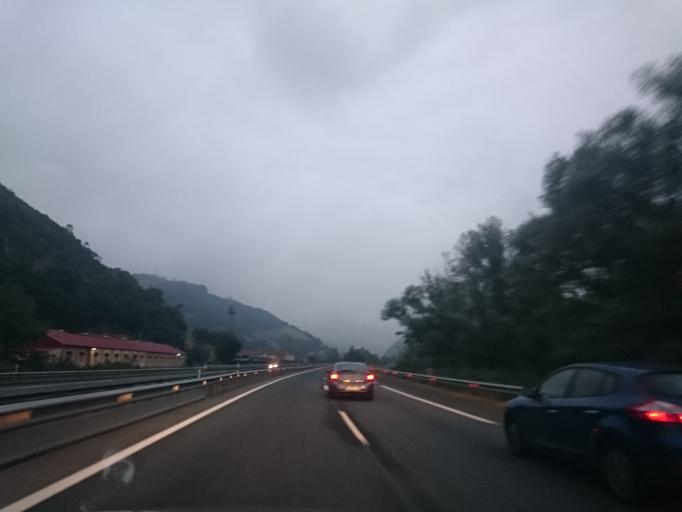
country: ES
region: Asturias
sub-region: Province of Asturias
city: Mieres
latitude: 43.2178
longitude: -5.7836
